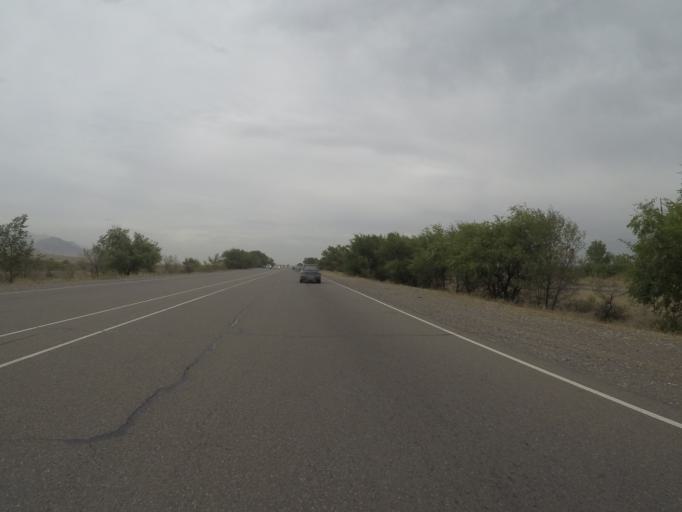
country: KG
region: Chuy
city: Tokmok
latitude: 42.8334
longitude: 75.4408
